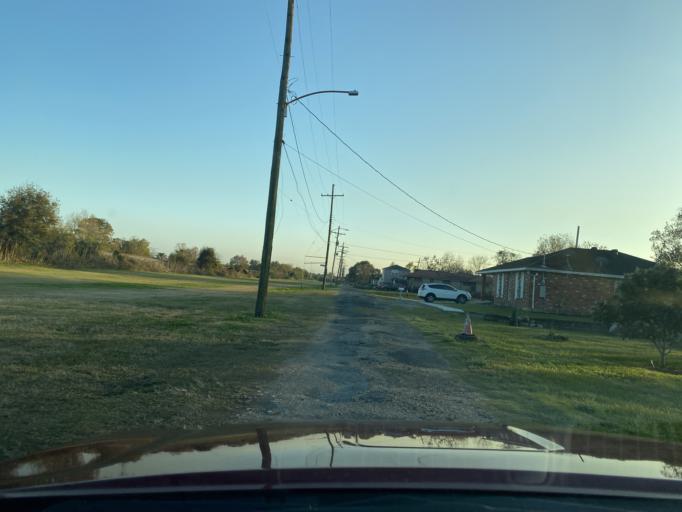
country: US
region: Louisiana
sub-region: Orleans Parish
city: New Orleans
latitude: 30.0214
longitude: -90.0474
